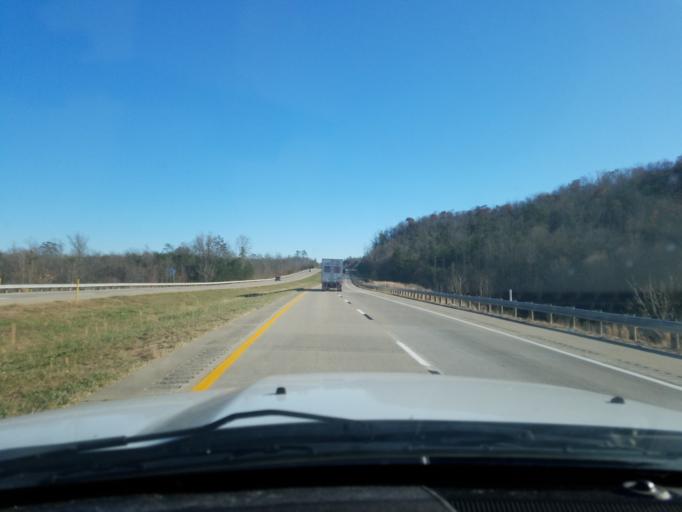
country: US
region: West Virginia
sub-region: Putnam County
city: Eleanor
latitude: 38.5395
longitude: -81.9633
